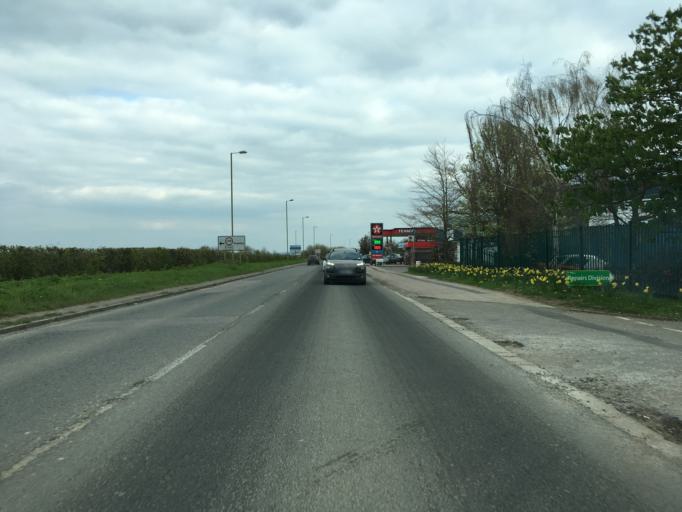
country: GB
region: England
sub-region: Oxfordshire
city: Witney
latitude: 51.7931
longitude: -1.5190
